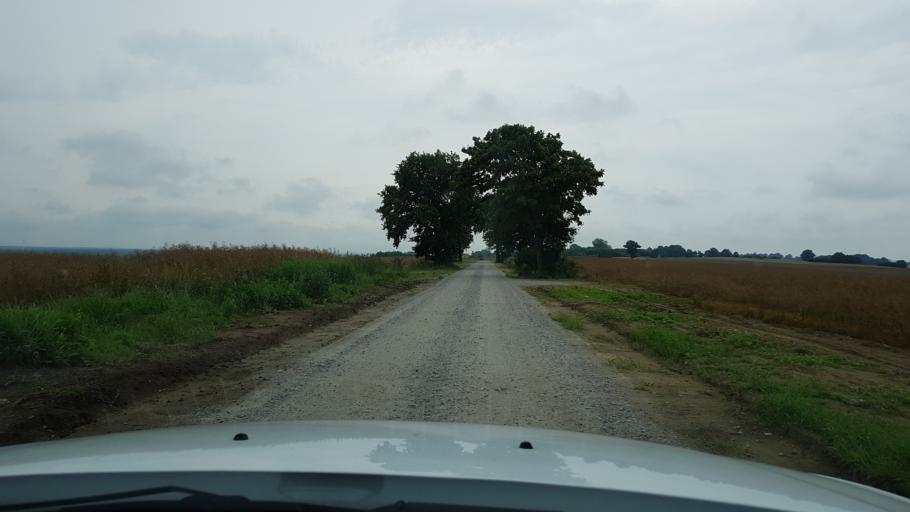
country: PL
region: West Pomeranian Voivodeship
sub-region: Powiat slawienski
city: Darlowo
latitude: 54.4642
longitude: 16.5013
